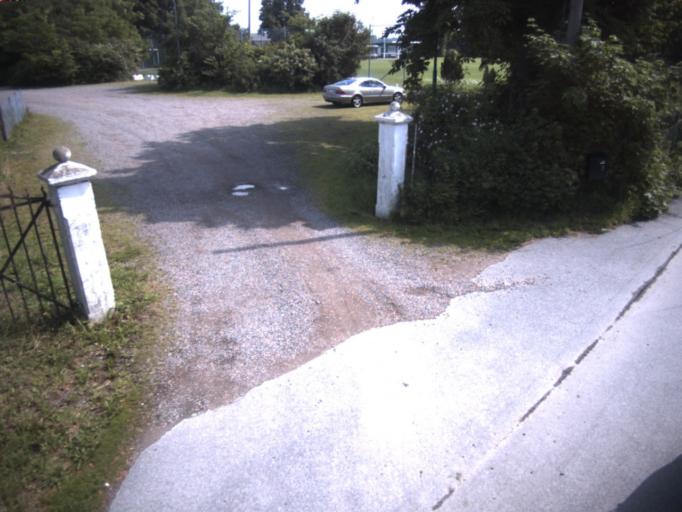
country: SE
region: Skane
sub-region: Angelholms Kommun
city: Strovelstorp
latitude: 56.1394
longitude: 12.8152
